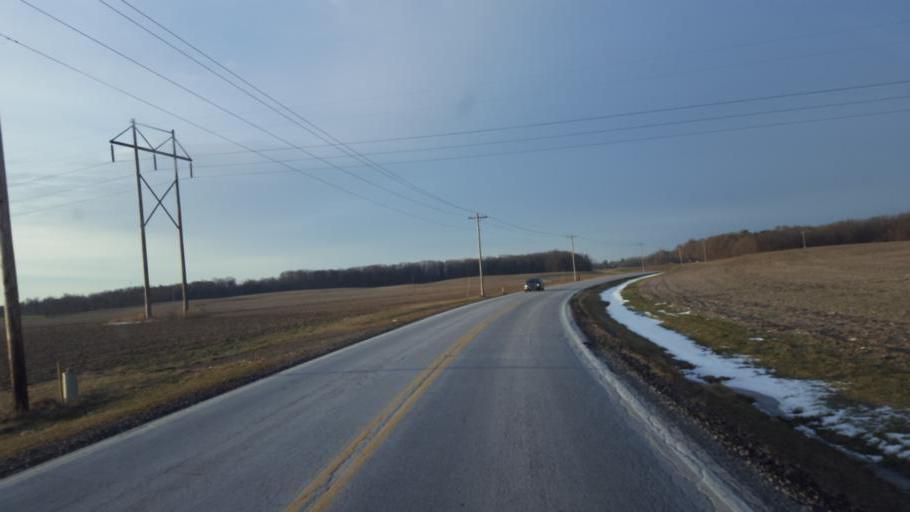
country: US
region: Ohio
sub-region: Knox County
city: Centerburg
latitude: 40.4232
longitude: -82.6995
